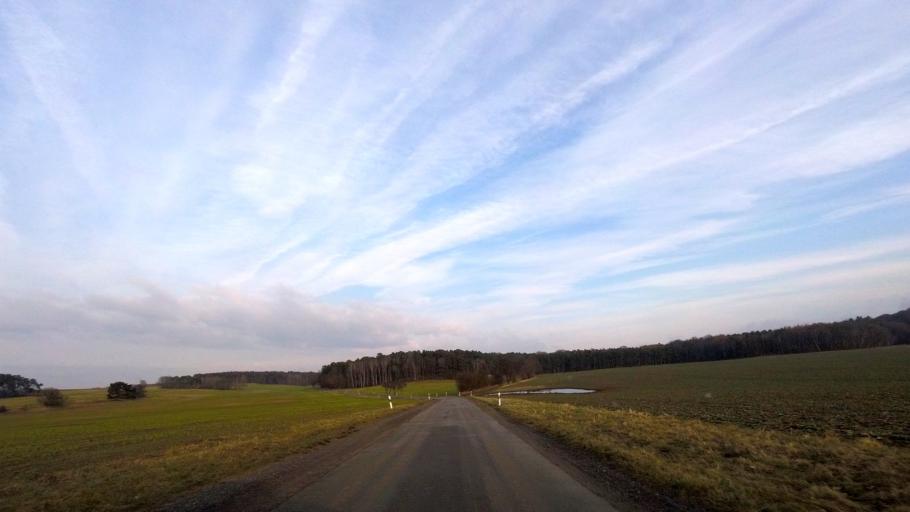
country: DE
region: Brandenburg
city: Wiesenburg
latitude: 52.1333
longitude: 12.4551
